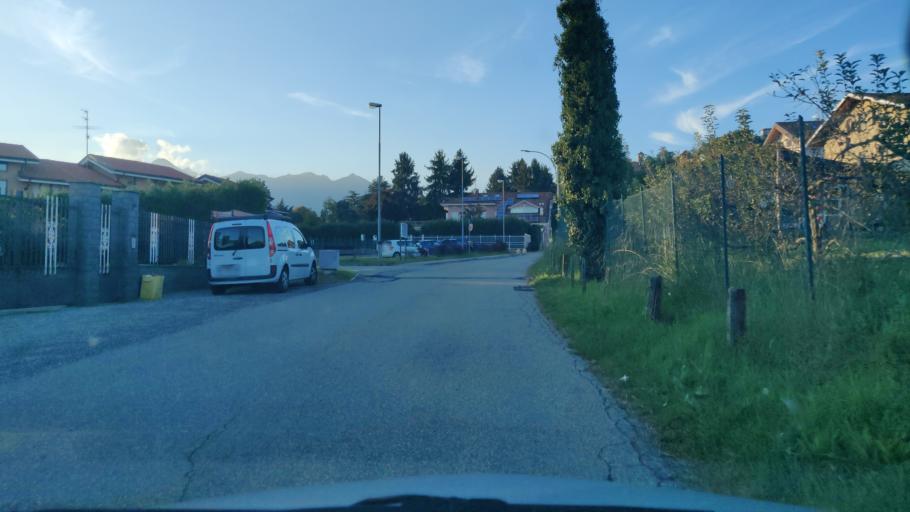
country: IT
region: Piedmont
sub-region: Provincia di Biella
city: Ronco Biellese
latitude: 45.5787
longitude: 8.0869
